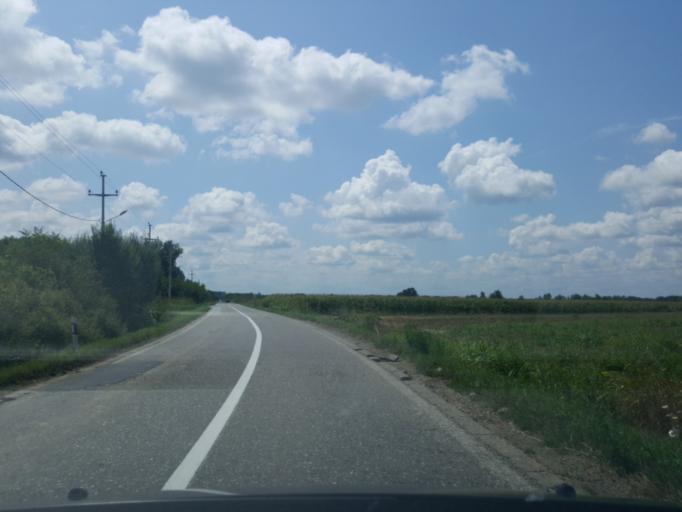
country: RS
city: Glusci
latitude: 44.8743
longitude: 19.5509
